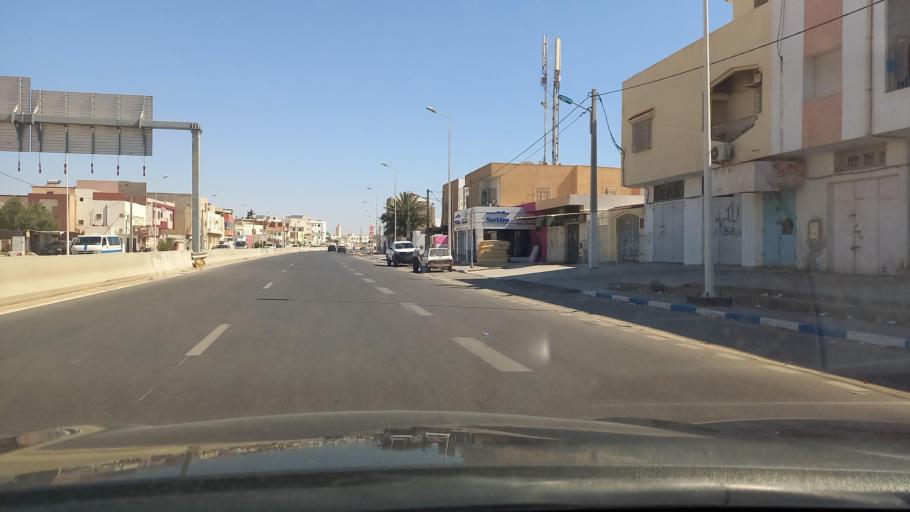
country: TN
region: Safaqis
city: Sfax
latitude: 34.7358
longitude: 10.7241
